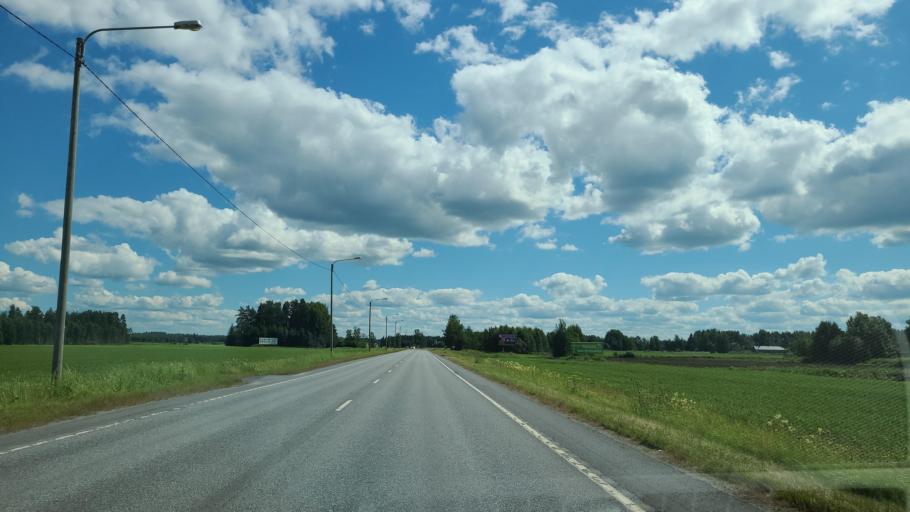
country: FI
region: Southern Ostrobothnia
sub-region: Seinaejoki
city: Ylistaro
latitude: 62.9152
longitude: 22.5683
